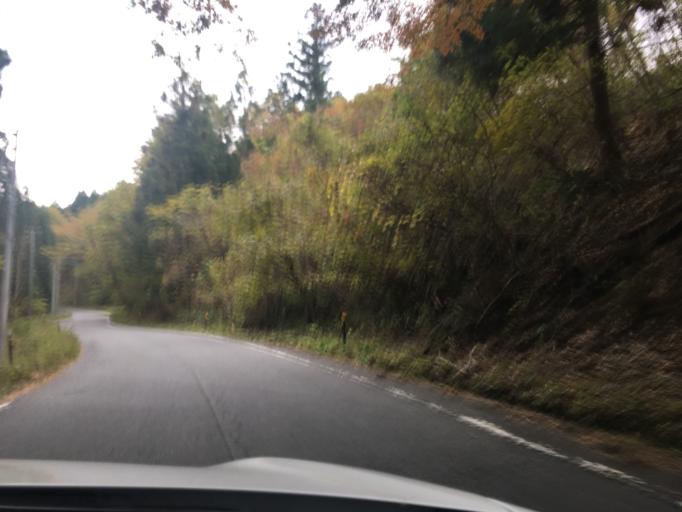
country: JP
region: Fukushima
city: Iwaki
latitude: 37.1163
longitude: 140.7792
